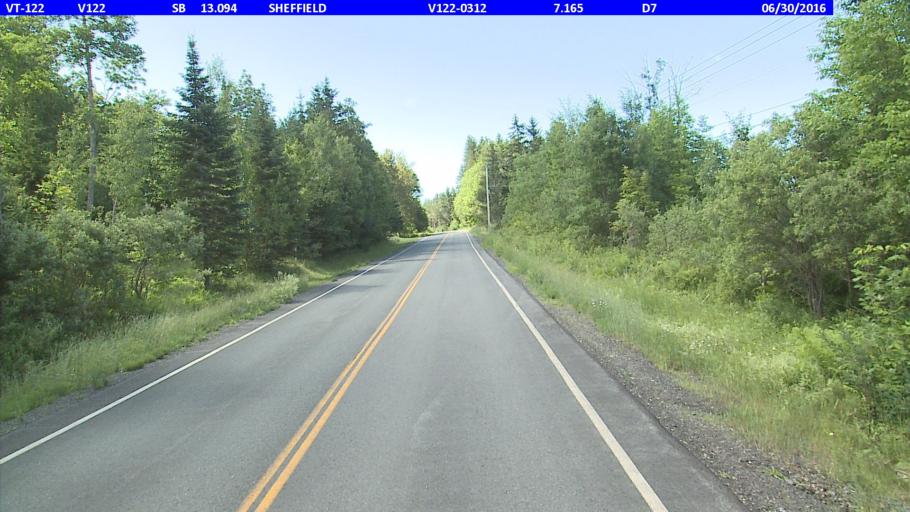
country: US
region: Vermont
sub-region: Caledonia County
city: Lyndonville
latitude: 44.6714
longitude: -72.1609
